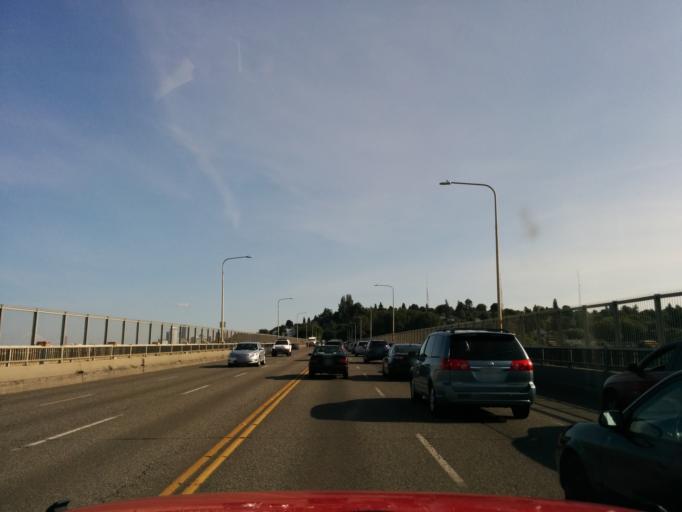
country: US
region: Washington
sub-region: King County
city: Seattle
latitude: 47.6484
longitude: -122.3473
